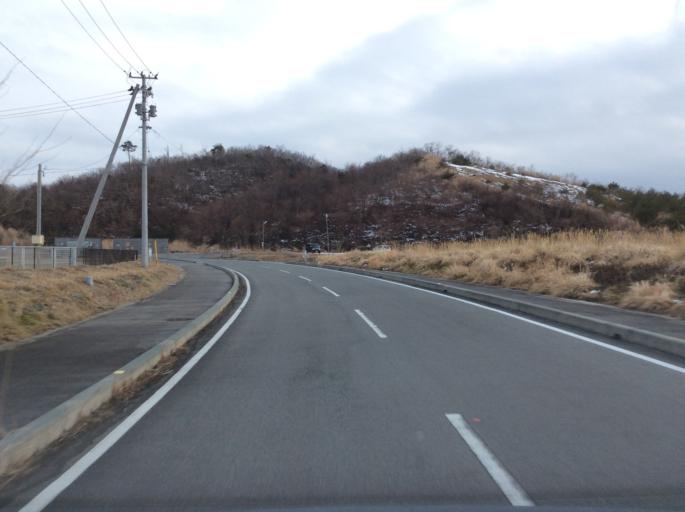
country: JP
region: Fukushima
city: Iwaki
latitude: 37.1252
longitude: 140.9648
